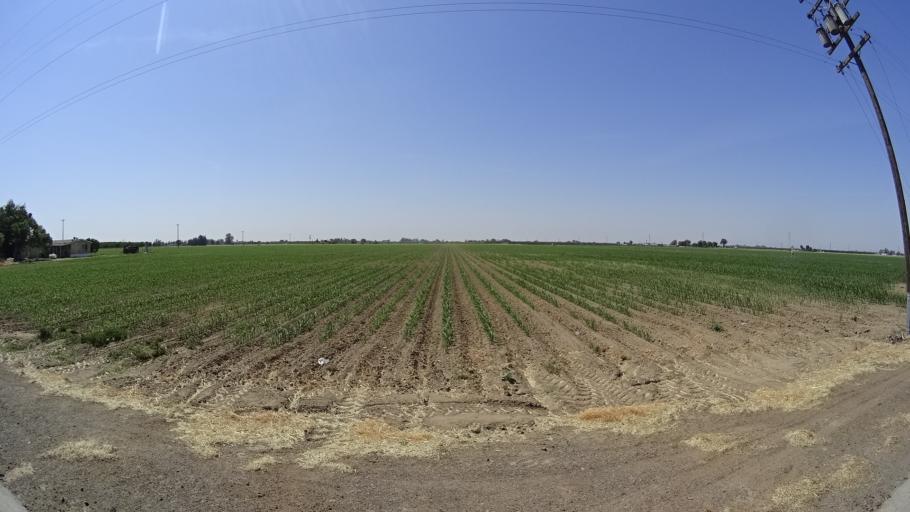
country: US
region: California
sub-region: Fresno County
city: Riverdale
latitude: 36.4019
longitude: -119.8818
